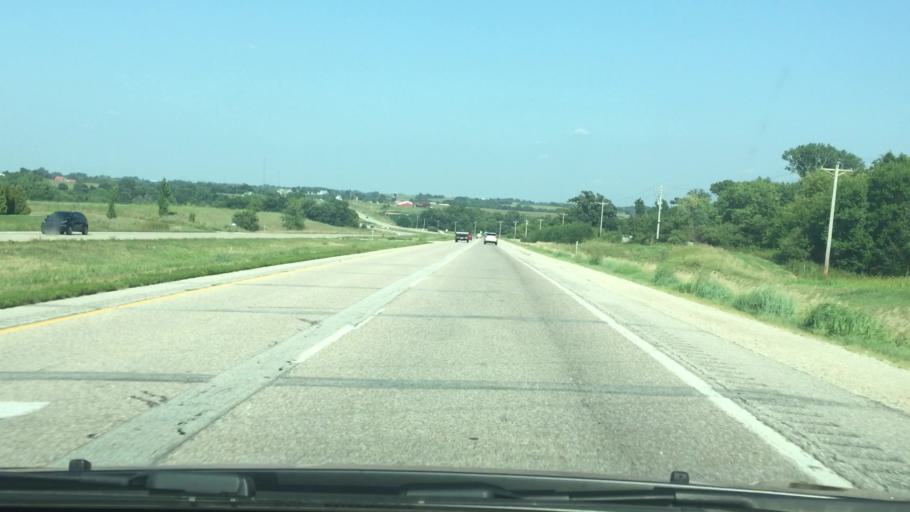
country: US
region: Iowa
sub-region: Cedar County
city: Durant
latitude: 41.5006
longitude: -90.9459
